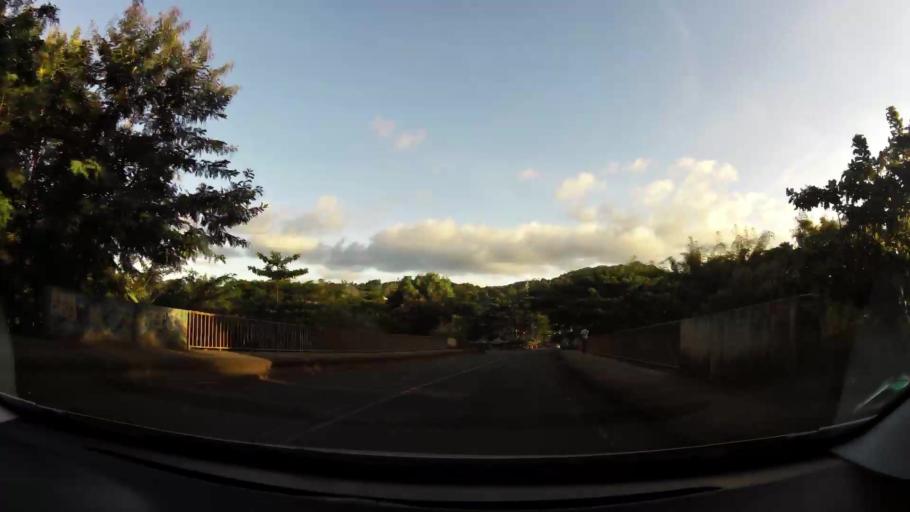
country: YT
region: Dembeni
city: Dembeni
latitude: -12.8414
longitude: 45.1844
